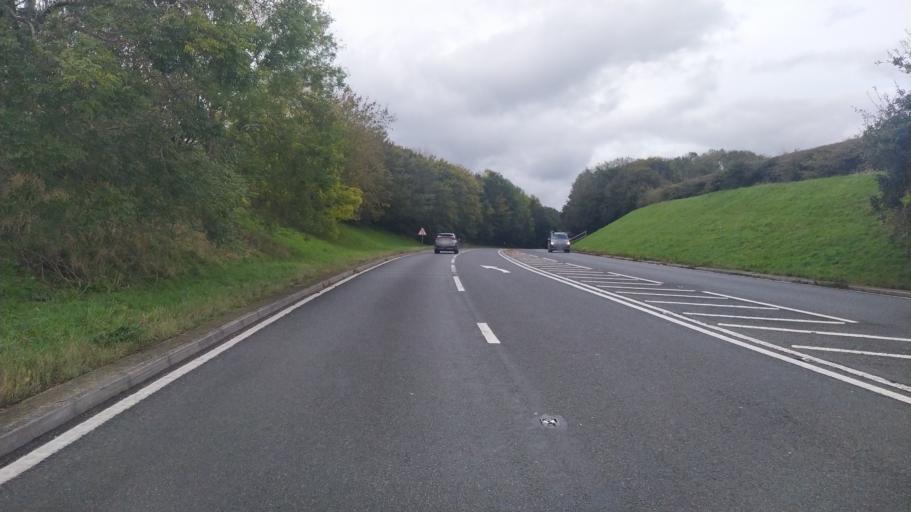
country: GB
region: England
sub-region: Dorset
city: Bridport
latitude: 50.7242
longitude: -2.7745
